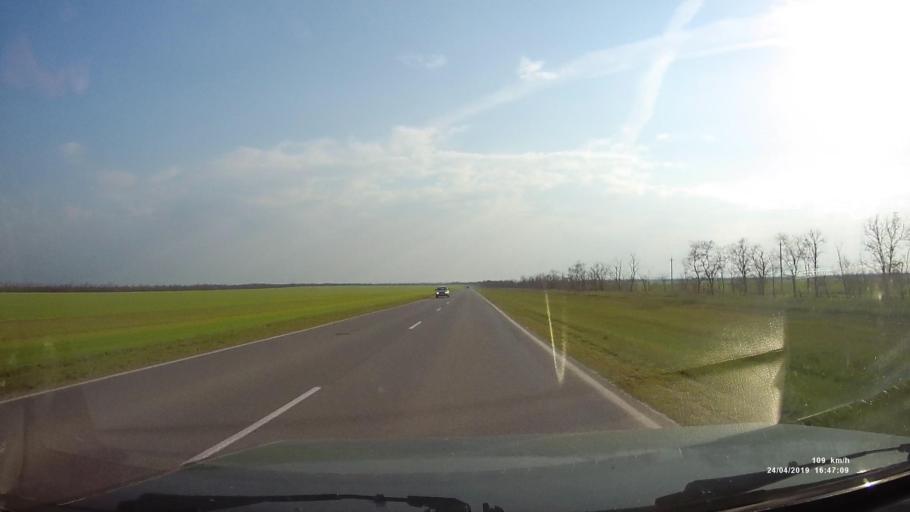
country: RU
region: Rostov
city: Proletarsk
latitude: 46.7478
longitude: 41.7914
